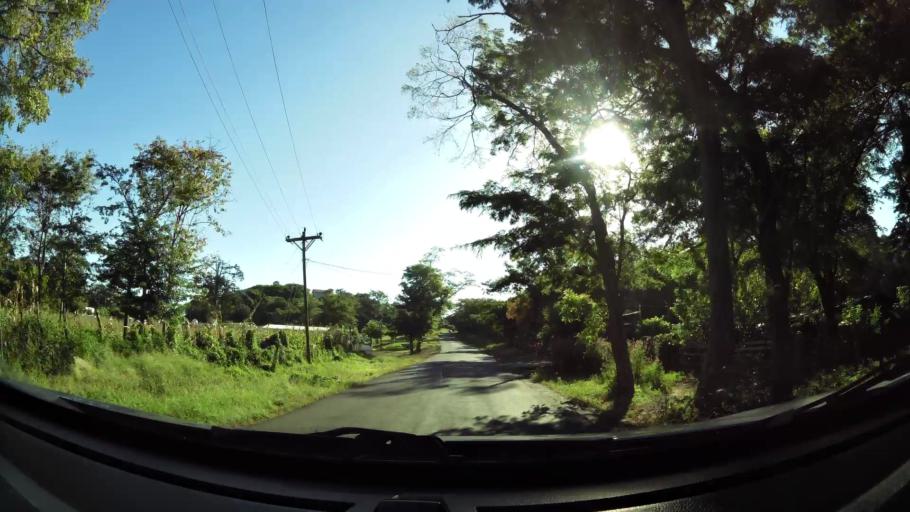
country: CR
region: Guanacaste
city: Sardinal
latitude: 10.4993
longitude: -85.6405
